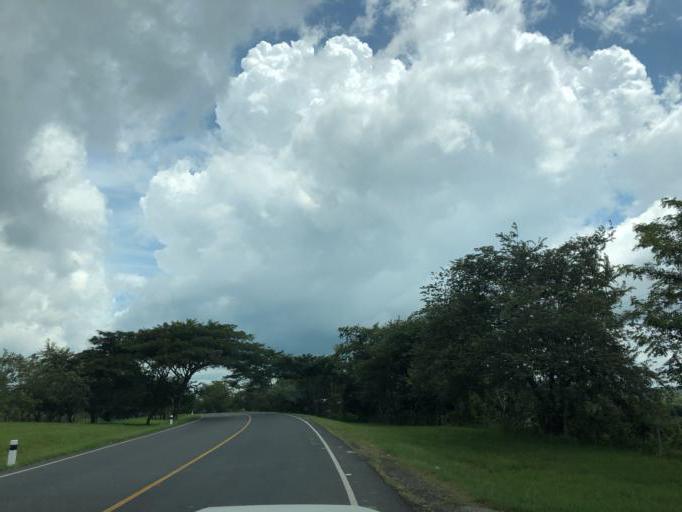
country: NI
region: Chontales
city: Santo Tomas
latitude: 12.0584
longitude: -85.0606
